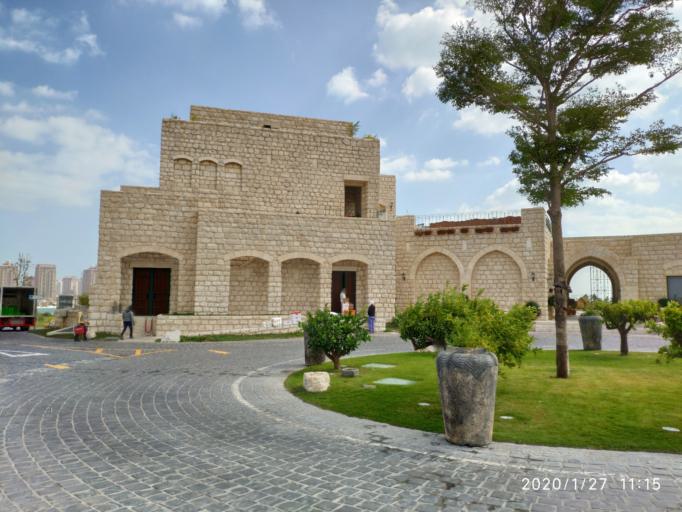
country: QA
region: Baladiyat ad Dawhah
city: Doha
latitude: 25.3635
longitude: 51.5247
